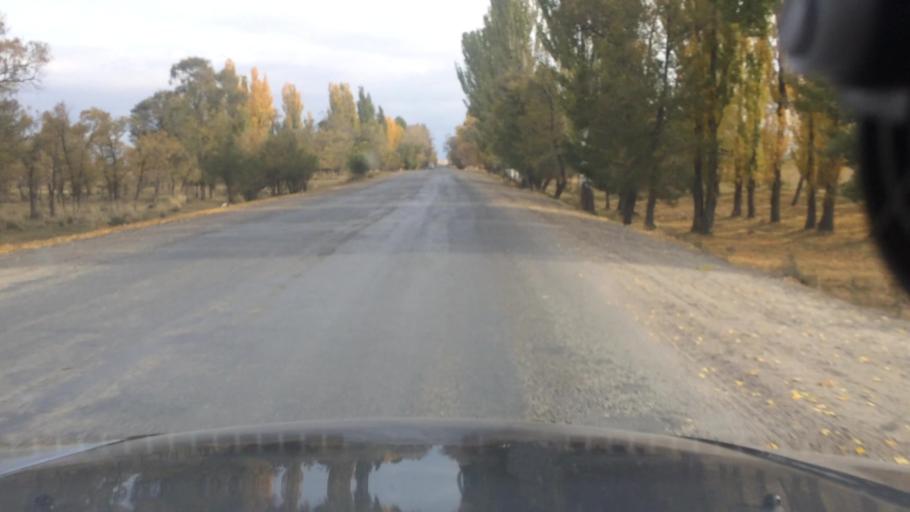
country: KG
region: Ysyk-Koel
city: Karakol
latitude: 42.5408
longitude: 78.3845
